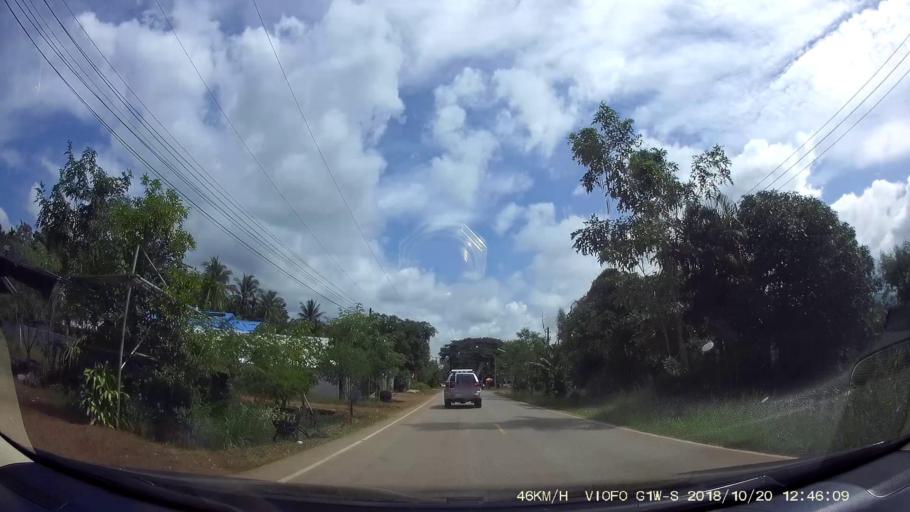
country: TH
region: Chaiyaphum
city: Khon San
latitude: 16.5344
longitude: 101.8784
